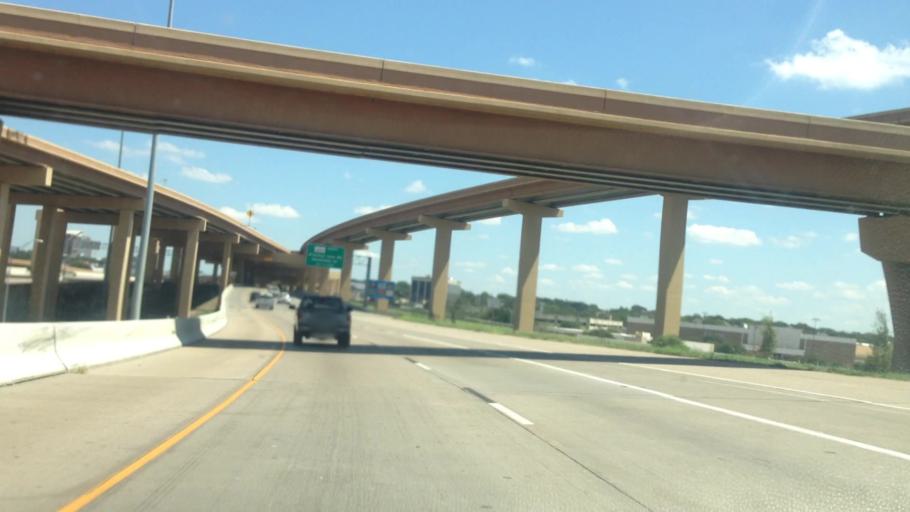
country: US
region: Texas
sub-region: Tarrant County
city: North Richland Hills
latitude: 32.8319
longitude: -97.2045
